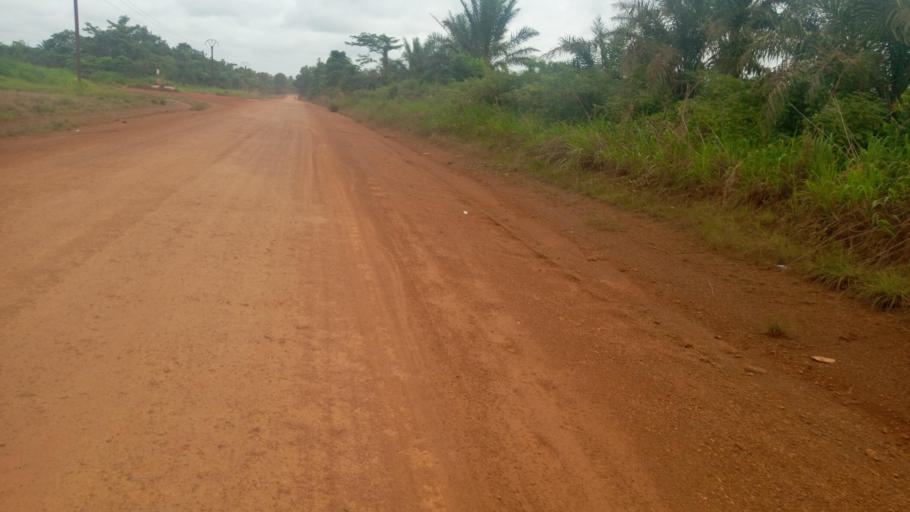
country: SL
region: Southern Province
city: Mogbwemo
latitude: 7.7432
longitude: -12.2902
